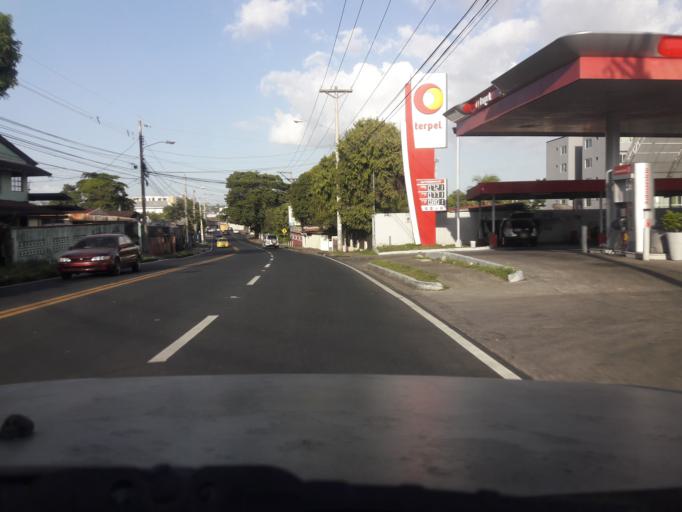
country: PA
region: Panama
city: Panama
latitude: 9.0161
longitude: -79.5045
